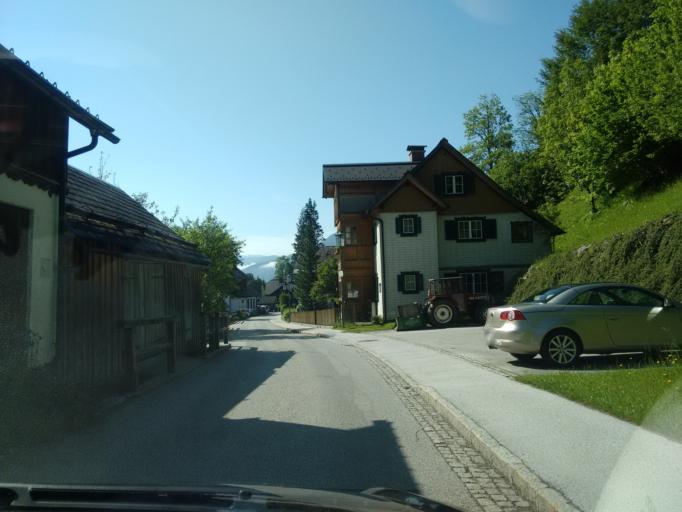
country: AT
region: Styria
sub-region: Politischer Bezirk Liezen
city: Altaussee
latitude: 47.6417
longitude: 13.7626
